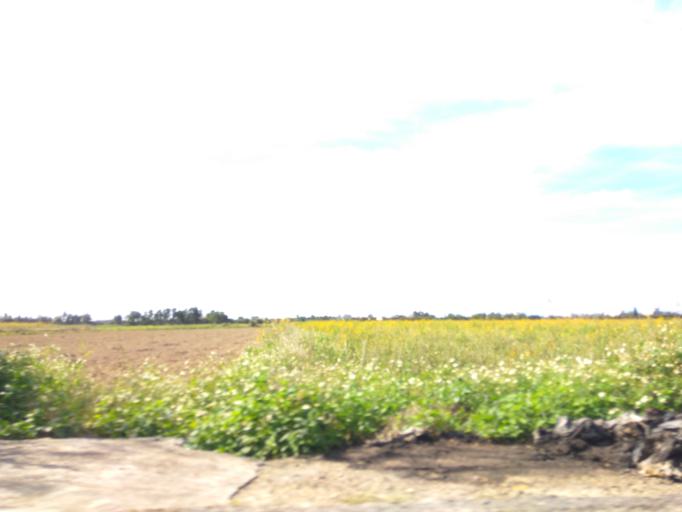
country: TW
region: Taiwan
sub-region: Hsinchu
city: Zhubei
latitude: 25.0163
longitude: 121.0665
